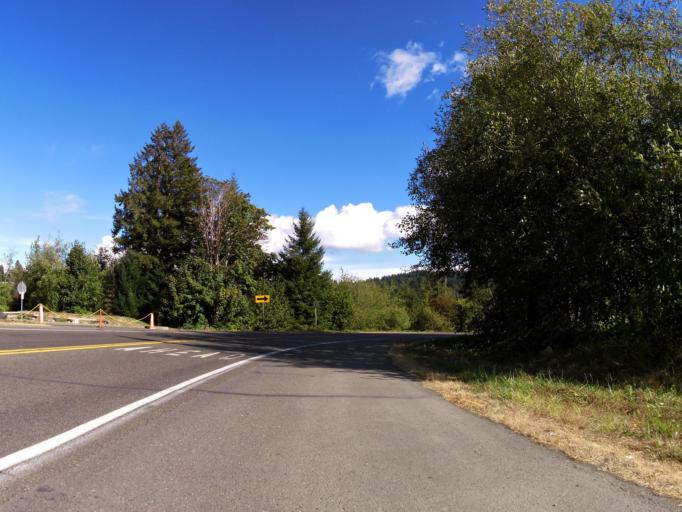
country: US
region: Washington
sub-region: Thurston County
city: Olympia
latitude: 47.0476
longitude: -122.9927
